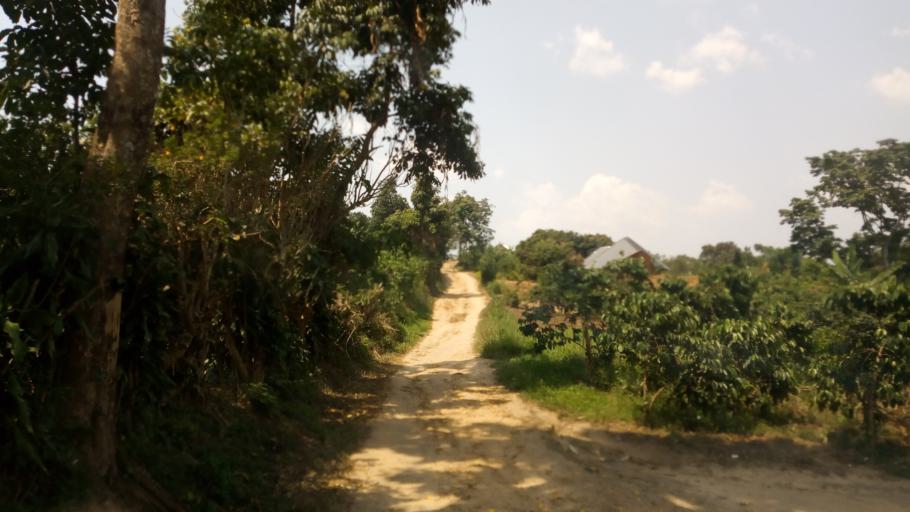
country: UG
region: Western Region
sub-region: Kanungu District
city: Ntungamo
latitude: -0.8053
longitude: 29.6476
